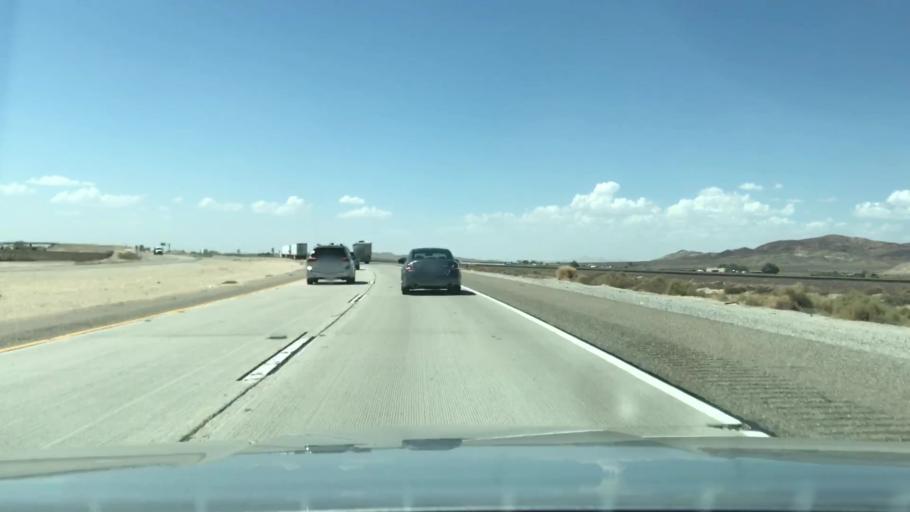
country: US
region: California
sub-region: San Bernardino County
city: Lenwood
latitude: 34.9120
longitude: -117.0990
